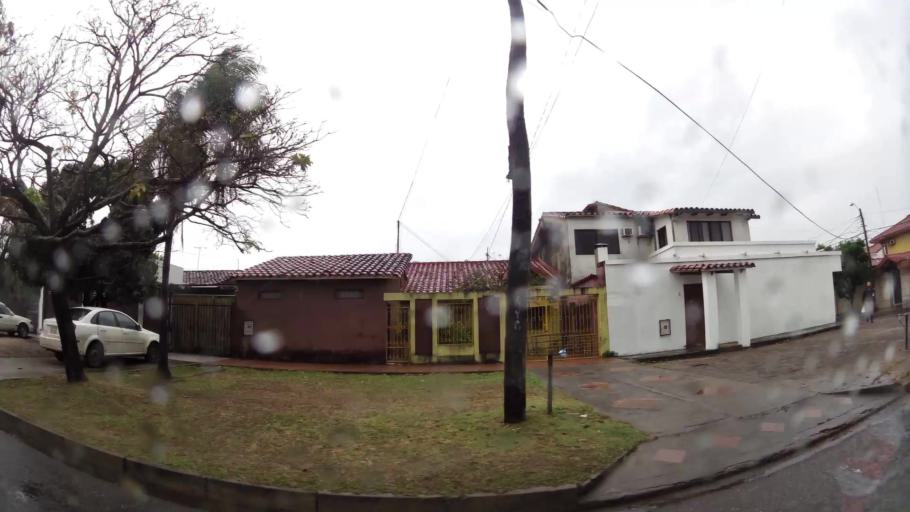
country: BO
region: Santa Cruz
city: Santa Cruz de la Sierra
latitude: -17.7695
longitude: -63.1506
